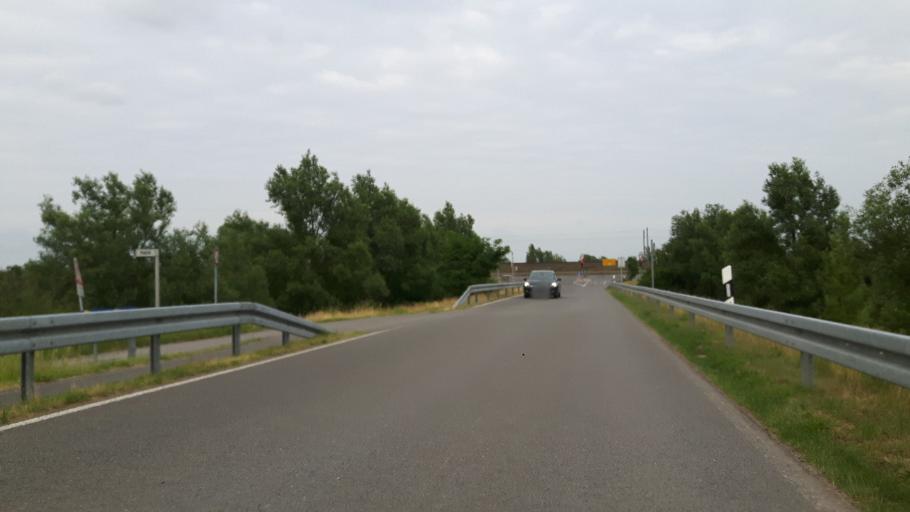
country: DE
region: Saxony-Anhalt
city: Wittenburg
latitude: 51.8528
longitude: 12.6478
